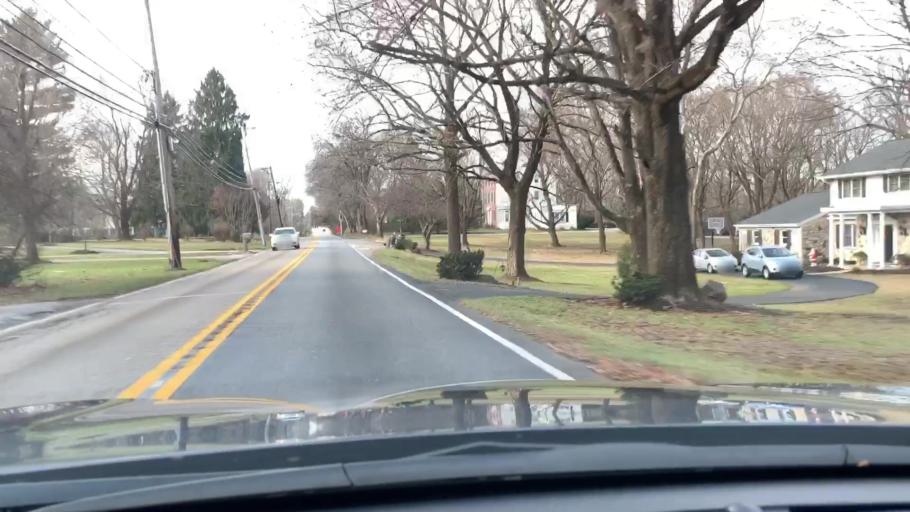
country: US
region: Pennsylvania
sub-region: Delaware County
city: Wayne
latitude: 39.9993
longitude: -75.4039
